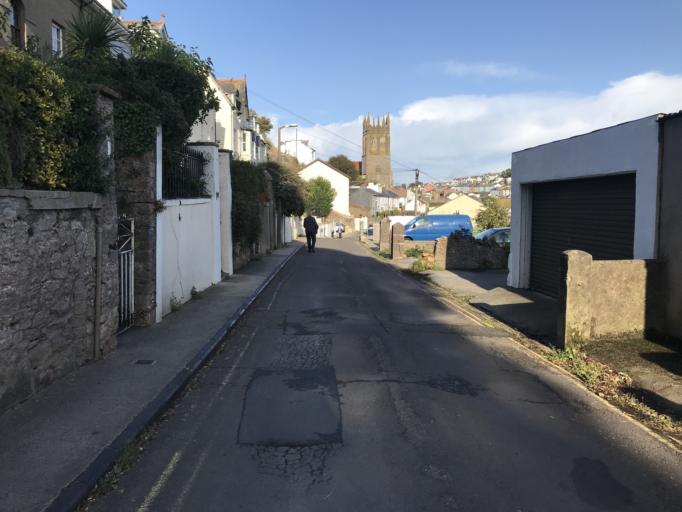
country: GB
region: England
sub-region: Borough of Torbay
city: Brixham
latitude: 50.3946
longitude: -3.5186
